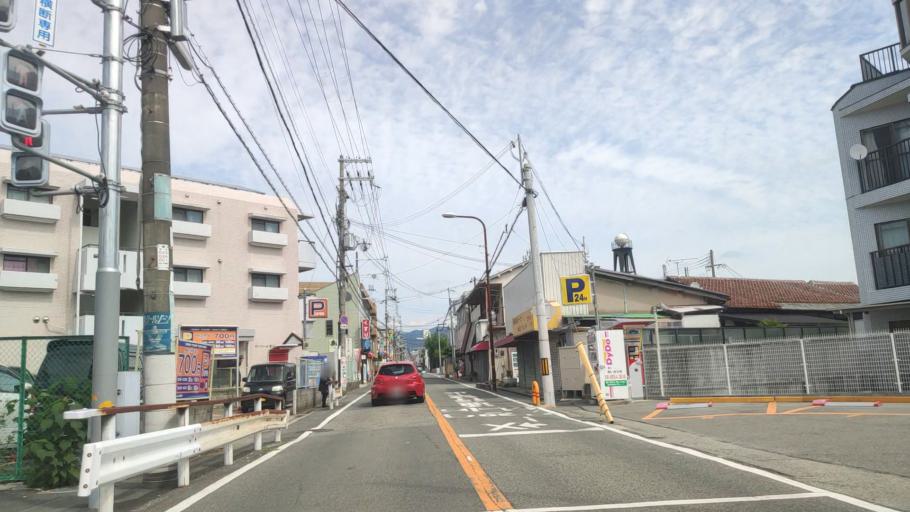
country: JP
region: Osaka
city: Toyonaka
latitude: 34.8037
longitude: 135.4640
